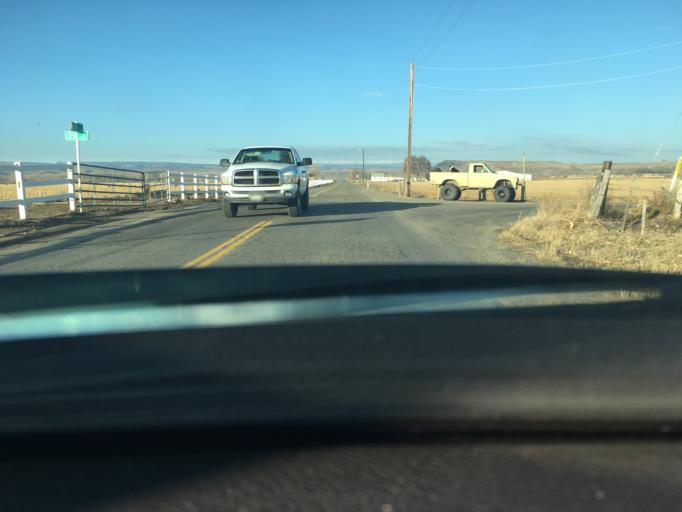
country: US
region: Colorado
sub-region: Delta County
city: Delta
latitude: 38.7483
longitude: -108.1293
